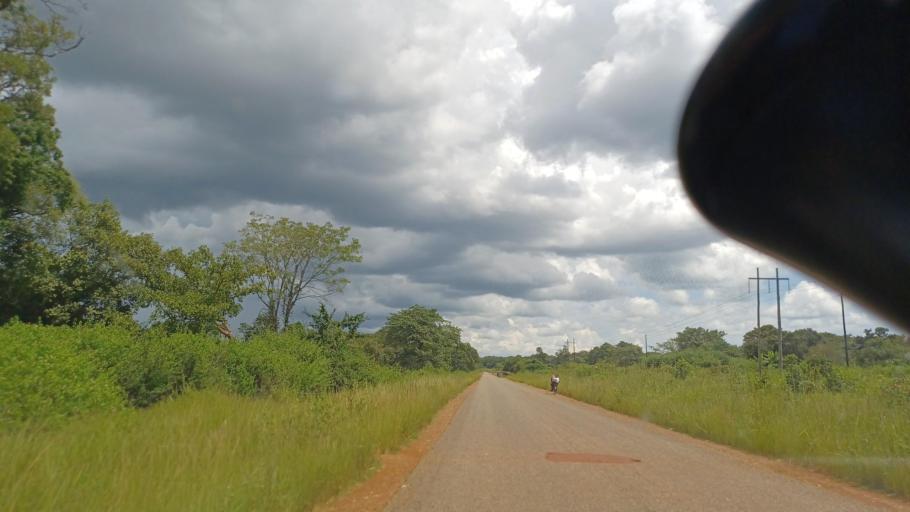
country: ZM
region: North-Western
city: Kasempa
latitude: -12.7737
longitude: 26.0128
